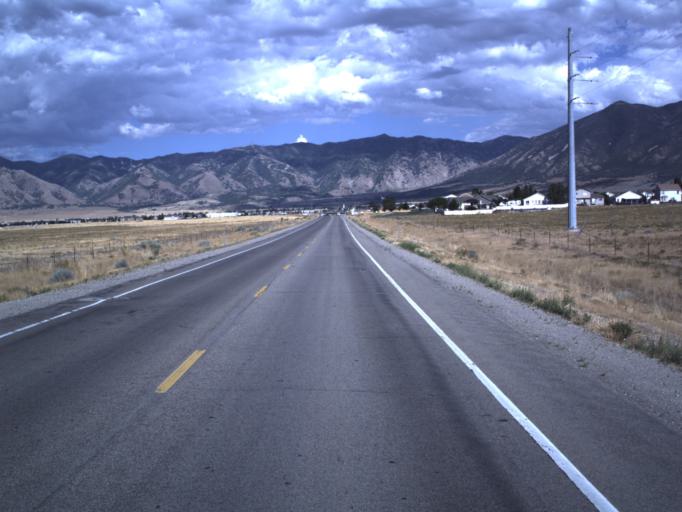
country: US
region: Utah
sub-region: Tooele County
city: Tooele
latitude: 40.5508
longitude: -112.3243
